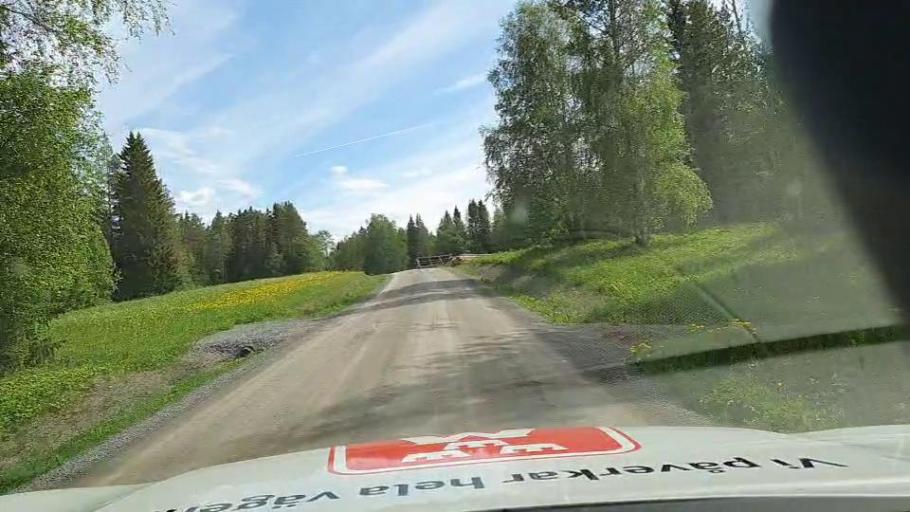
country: SE
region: Jaemtland
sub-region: OEstersunds Kommun
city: Brunflo
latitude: 63.0055
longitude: 14.7930
